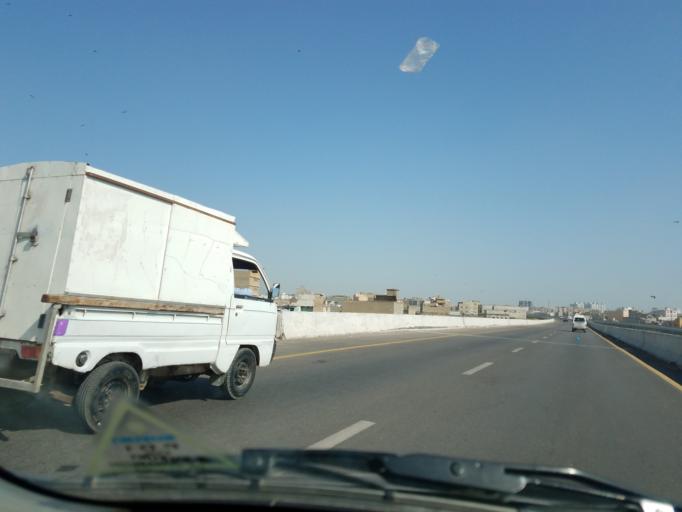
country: PK
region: Sindh
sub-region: Karachi District
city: Karachi
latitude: 24.8815
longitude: 67.0066
